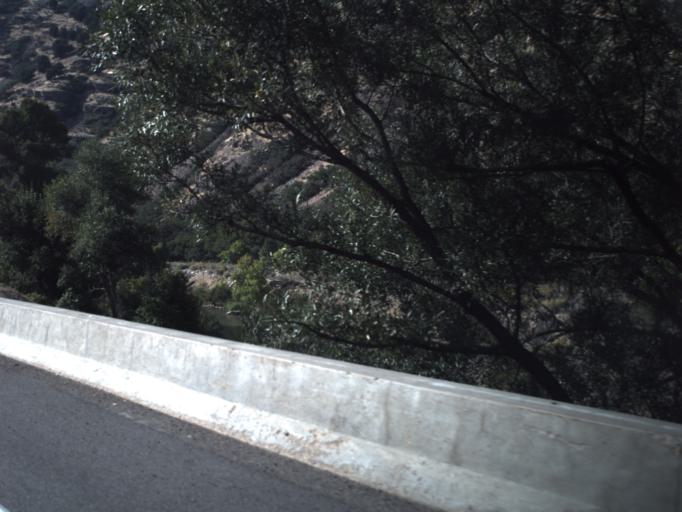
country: US
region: Utah
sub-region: Morgan County
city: Morgan
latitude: 41.0533
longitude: -111.5984
